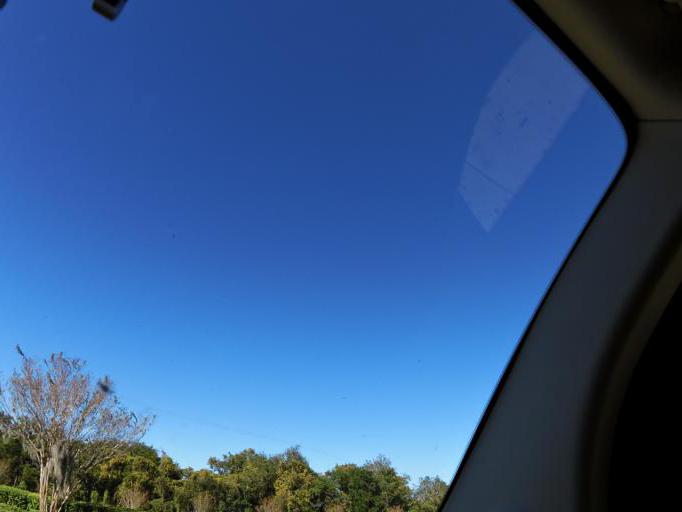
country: US
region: Florida
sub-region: Duval County
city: Jacksonville
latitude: 30.4115
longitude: -81.5620
